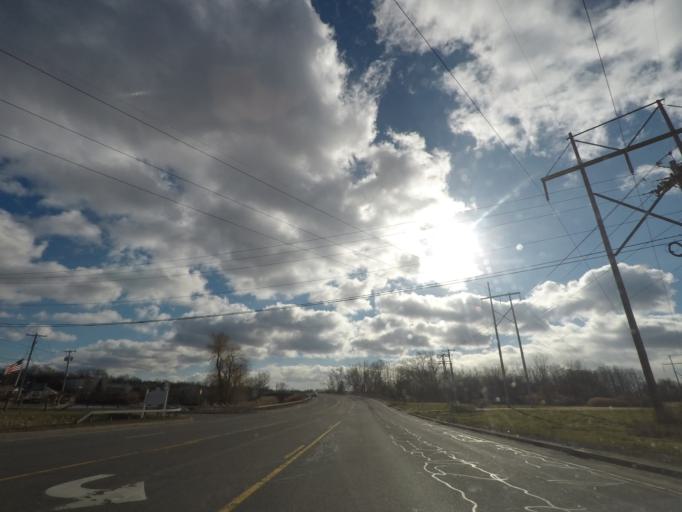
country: US
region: New York
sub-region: Schenectady County
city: Schenectady
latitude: 42.8321
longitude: -73.9316
